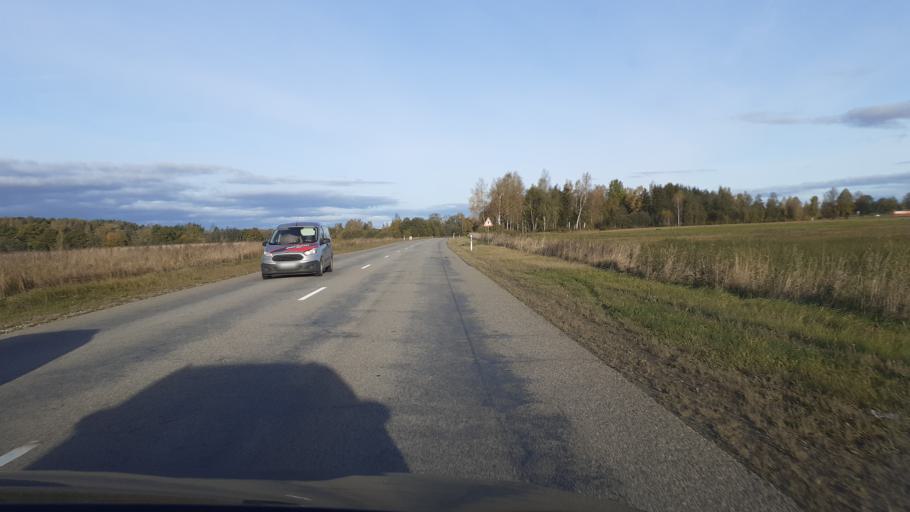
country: LV
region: Kuldigas Rajons
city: Kuldiga
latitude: 56.9367
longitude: 22.0303
